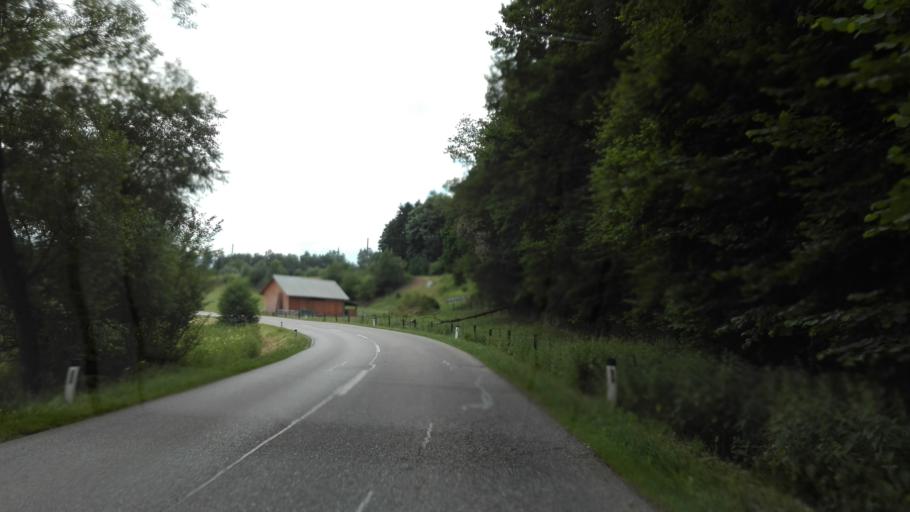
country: AT
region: Upper Austria
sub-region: Politischer Bezirk Urfahr-Umgebung
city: Engerwitzdorf
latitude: 48.2881
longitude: 14.4700
